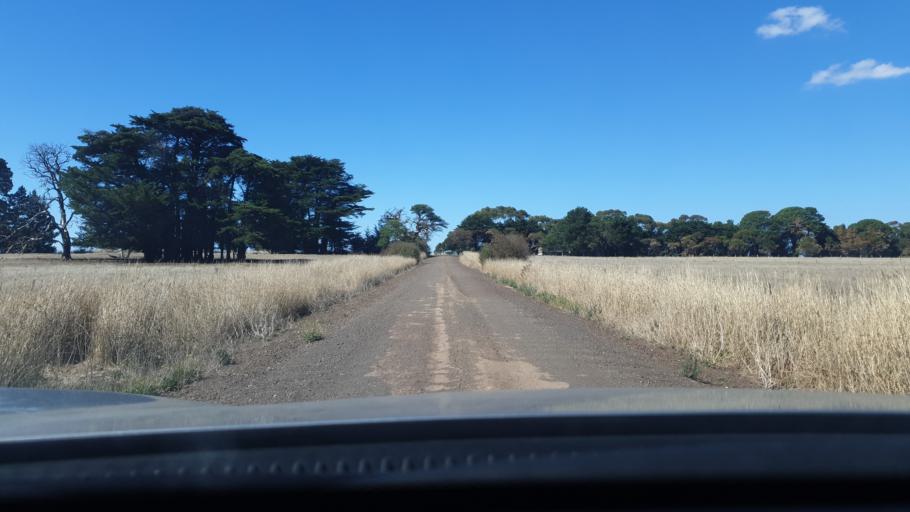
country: AU
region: Victoria
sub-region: Warrnambool
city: Warrnambool
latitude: -38.1647
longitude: 142.3944
